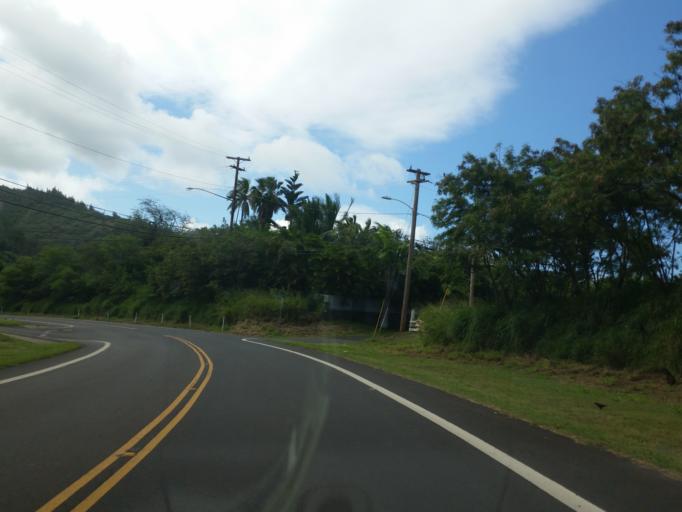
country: US
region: Hawaii
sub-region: Maui County
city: Waihee-Waiehu
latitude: 20.9431
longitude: -156.5138
